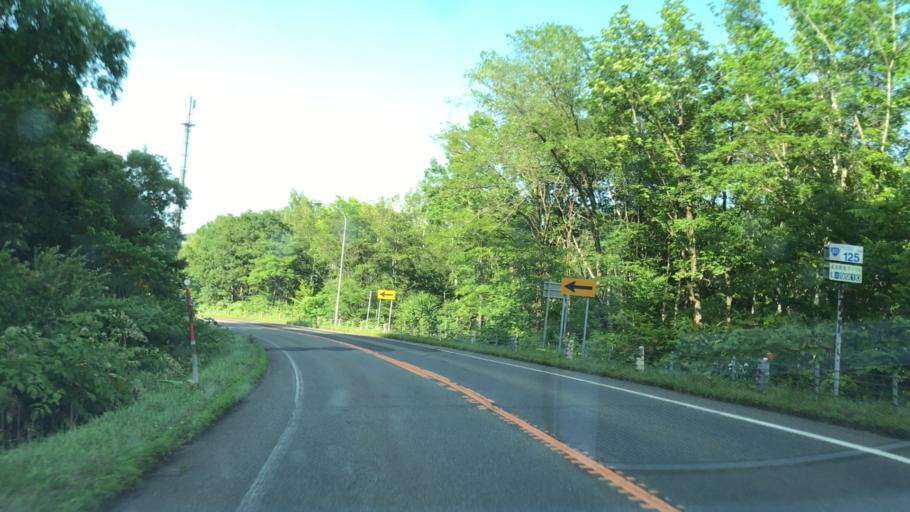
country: JP
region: Hokkaido
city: Shimo-furano
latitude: 42.8426
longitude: 142.4172
